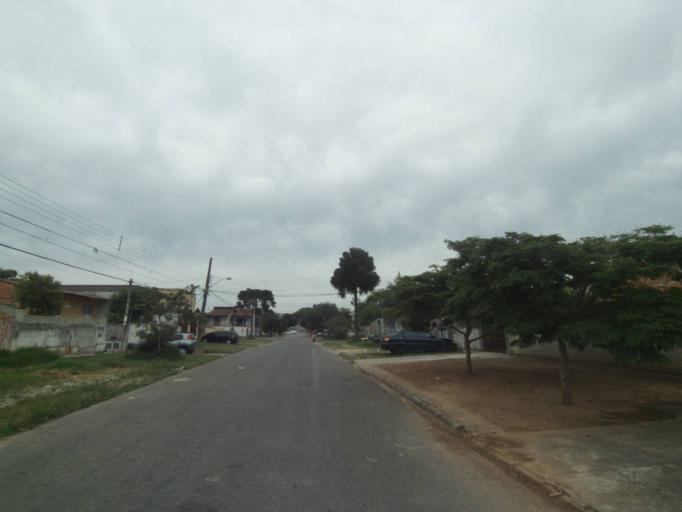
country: BR
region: Parana
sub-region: Pinhais
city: Pinhais
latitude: -25.4207
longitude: -49.1990
